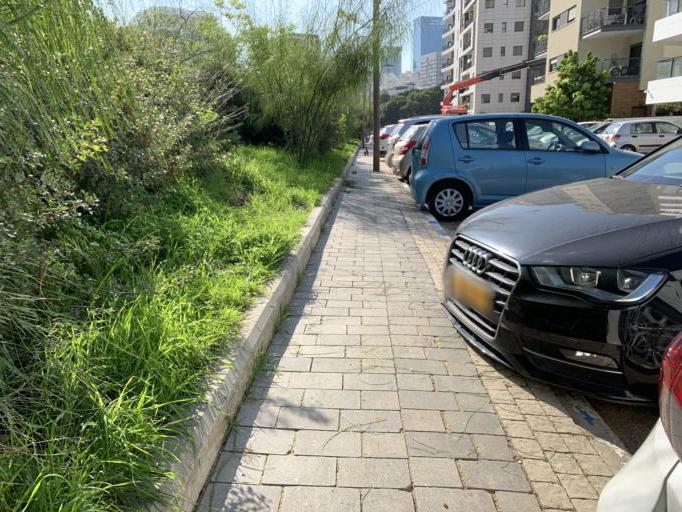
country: IL
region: Tel Aviv
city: Ramat Gan
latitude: 32.0909
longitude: 34.8070
